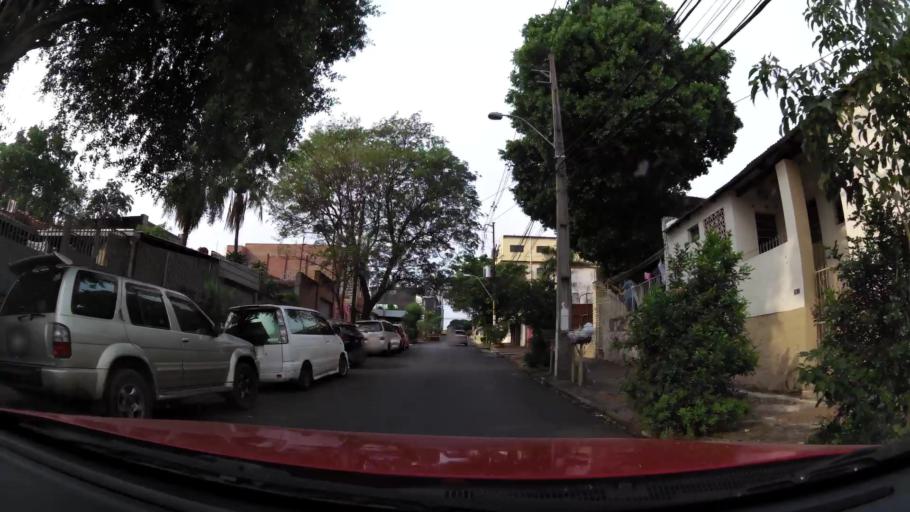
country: PY
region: Asuncion
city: Asuncion
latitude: -25.2993
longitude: -57.6186
